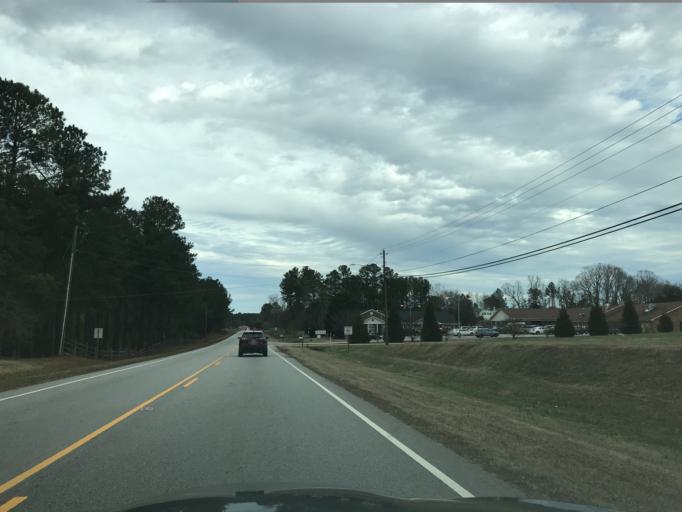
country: US
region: North Carolina
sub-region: Franklin County
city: Louisburg
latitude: 36.1187
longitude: -78.2941
